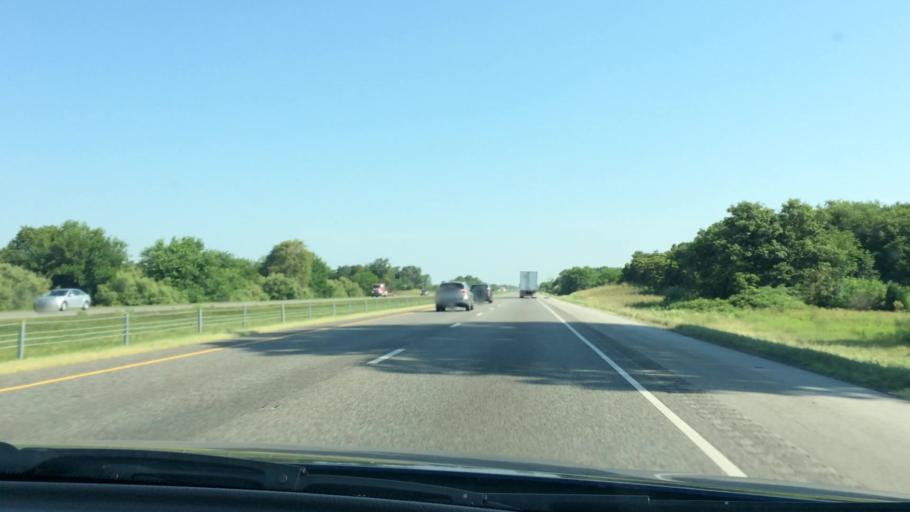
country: US
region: Indiana
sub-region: Newton County
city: Roselawn
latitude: 41.0933
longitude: -87.2651
